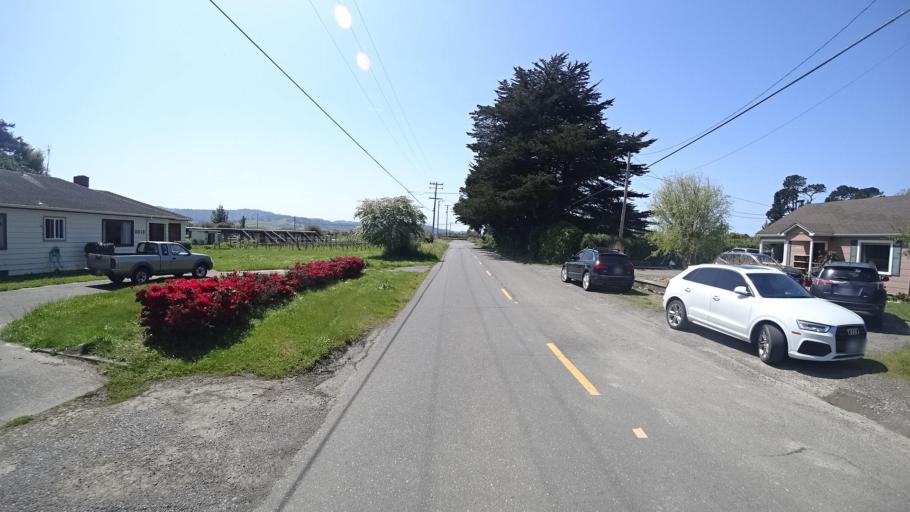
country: US
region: California
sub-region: Humboldt County
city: Fortuna
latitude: 40.5630
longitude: -124.1452
